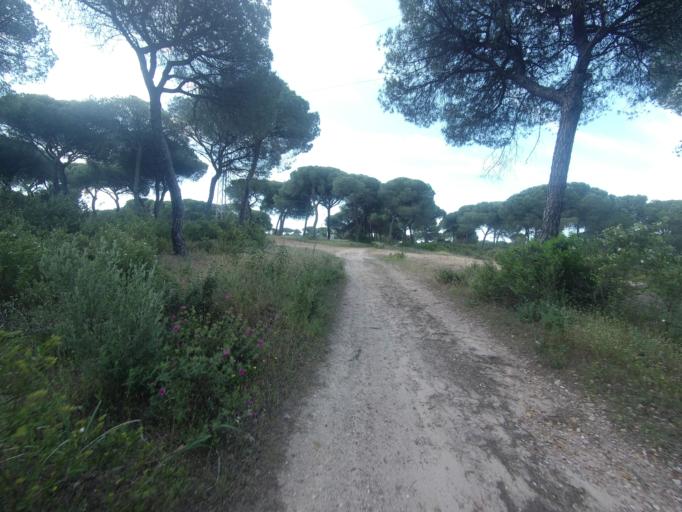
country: ES
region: Andalusia
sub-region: Provincia de Huelva
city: Aljaraque
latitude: 37.2318
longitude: -7.0627
